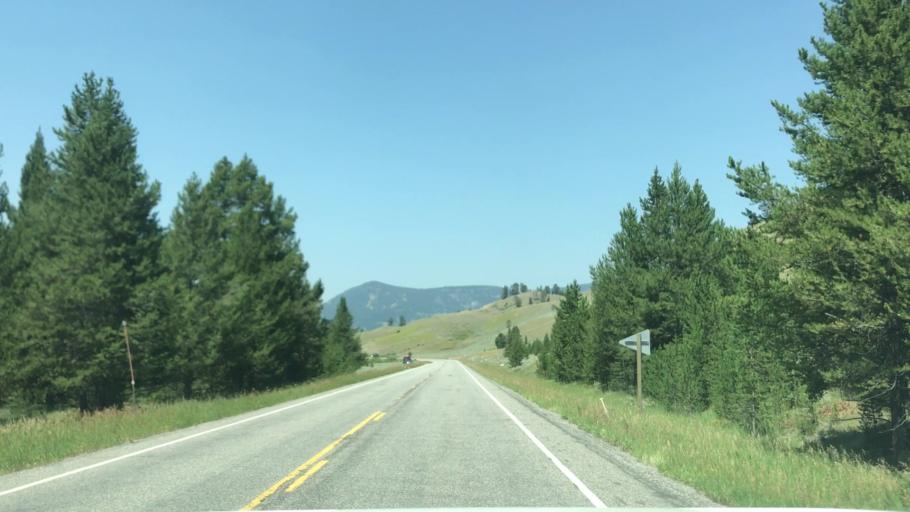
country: US
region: Montana
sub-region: Gallatin County
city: Big Sky
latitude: 45.0364
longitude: -111.1162
